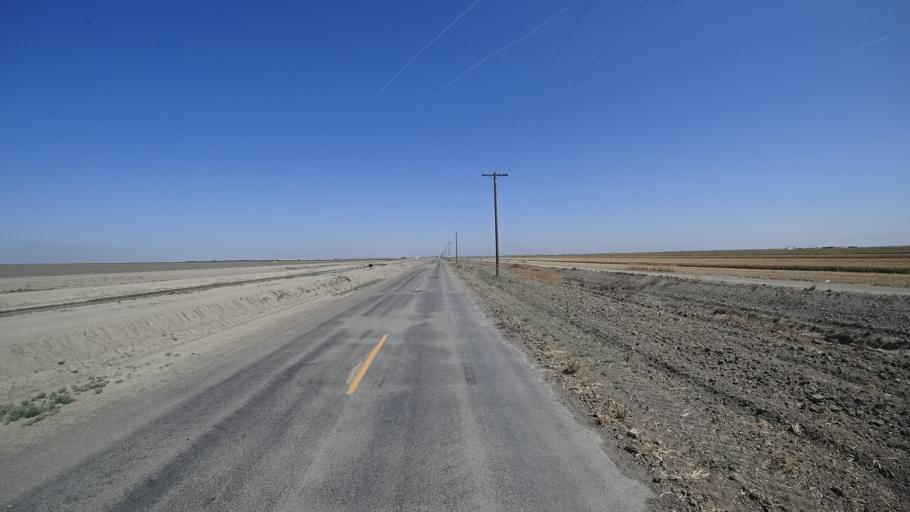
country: US
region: California
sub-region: Tulare County
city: Alpaugh
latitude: 35.9811
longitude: -119.5360
